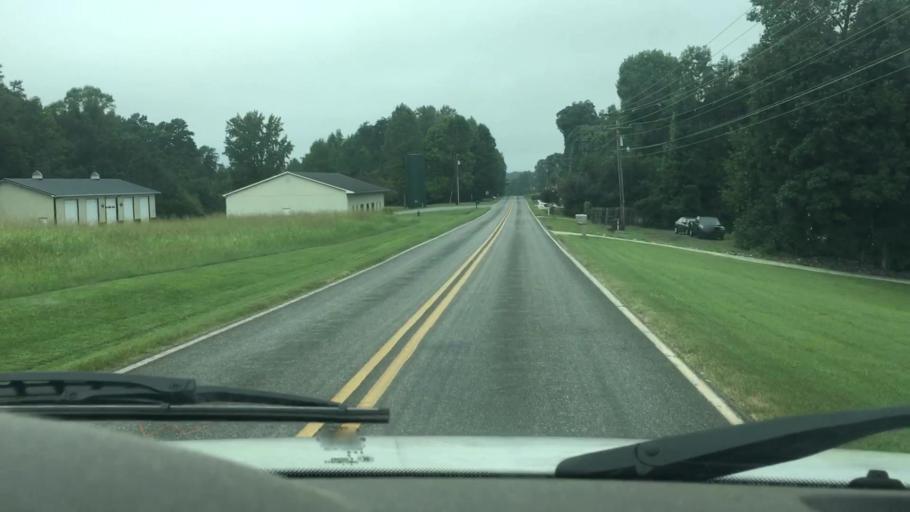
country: US
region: North Carolina
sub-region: Gaston County
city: Davidson
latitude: 35.5203
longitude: -80.8023
